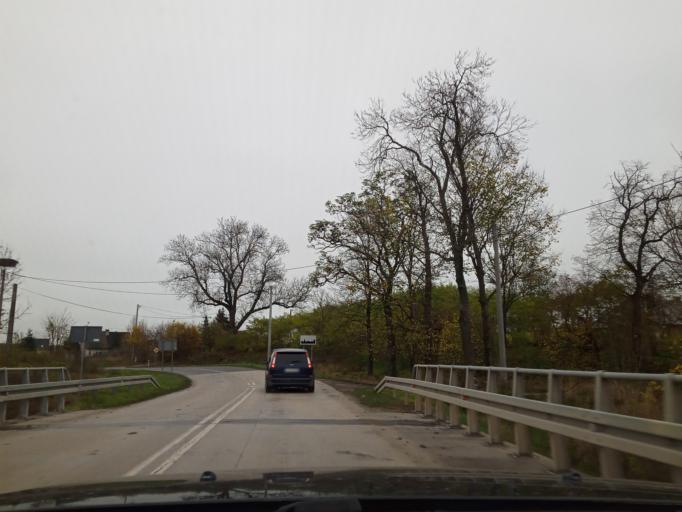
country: PL
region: Swietokrzyskie
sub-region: Powiat jedrzejowski
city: Jedrzejow
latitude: 50.5165
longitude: 20.3229
